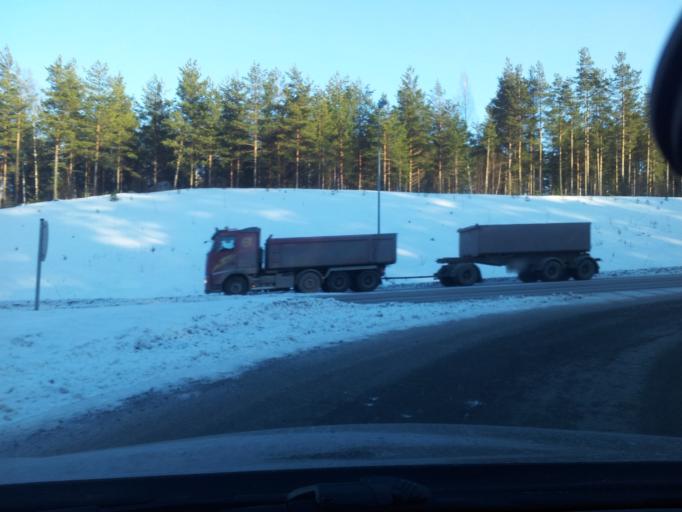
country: FI
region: Uusimaa
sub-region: Helsinki
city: Vihti
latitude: 60.3522
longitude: 24.3287
